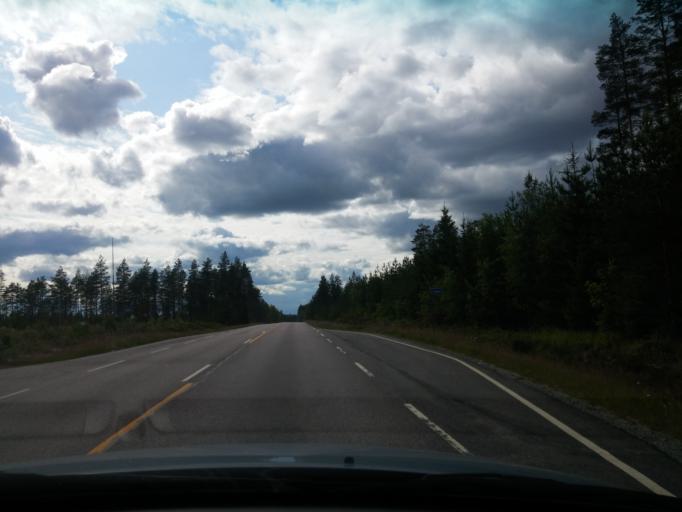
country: FI
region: Central Finland
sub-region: Saarijaervi-Viitasaari
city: Pylkoenmaeki
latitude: 62.6128
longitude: 24.7095
